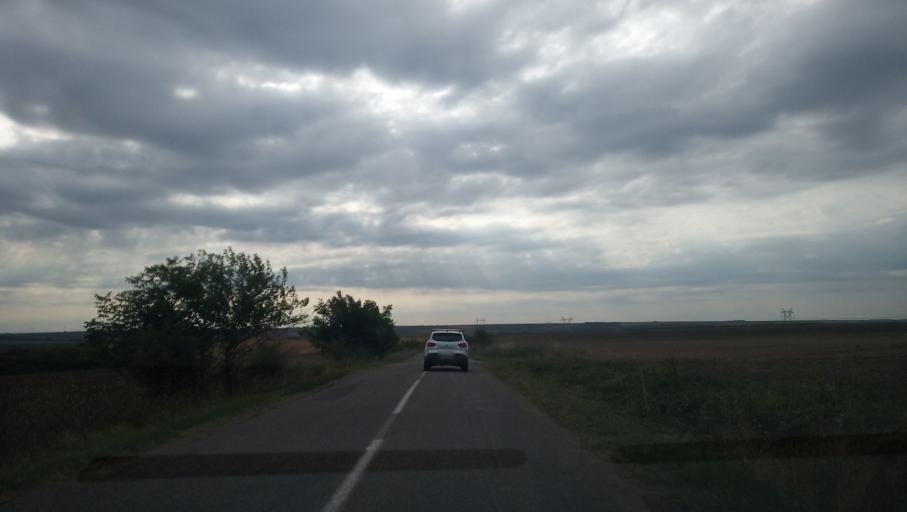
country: RO
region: Constanta
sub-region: Comuna Adamclisi
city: Adamclisi
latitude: 44.0278
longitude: 27.9885
